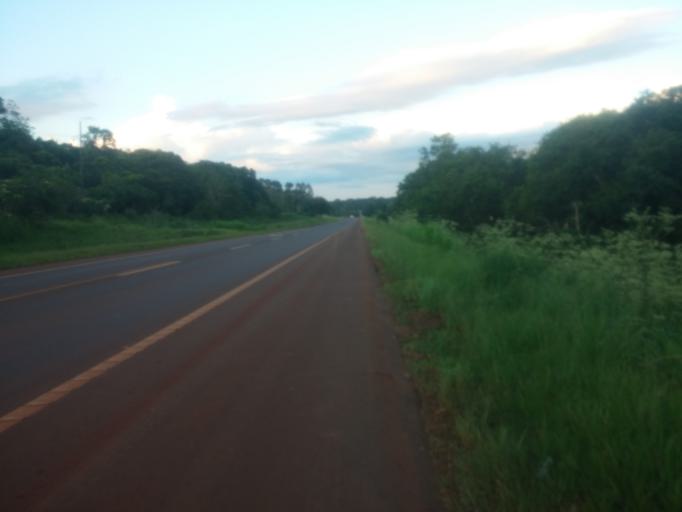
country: AR
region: Misiones
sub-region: Departamento de Obera
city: Obera
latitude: -27.4547
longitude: -55.0848
